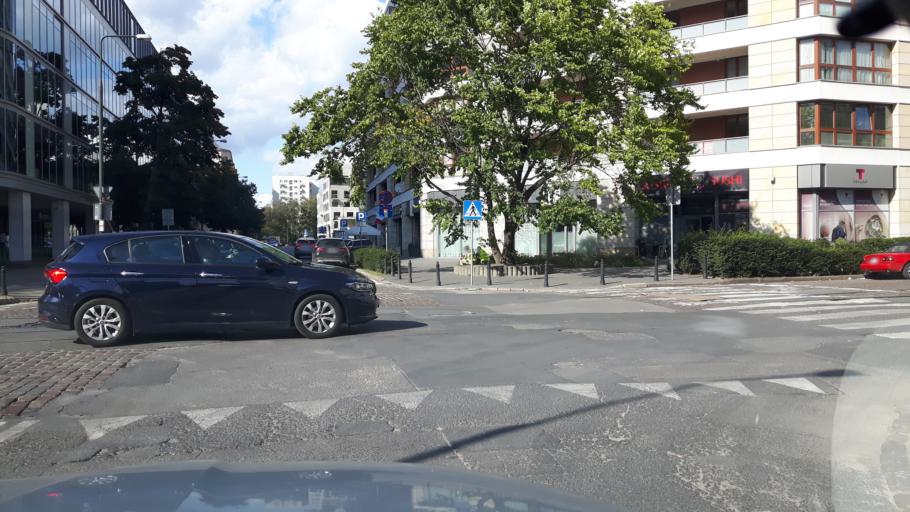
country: PL
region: Masovian Voivodeship
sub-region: Warszawa
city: Wola
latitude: 52.2360
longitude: 20.9846
